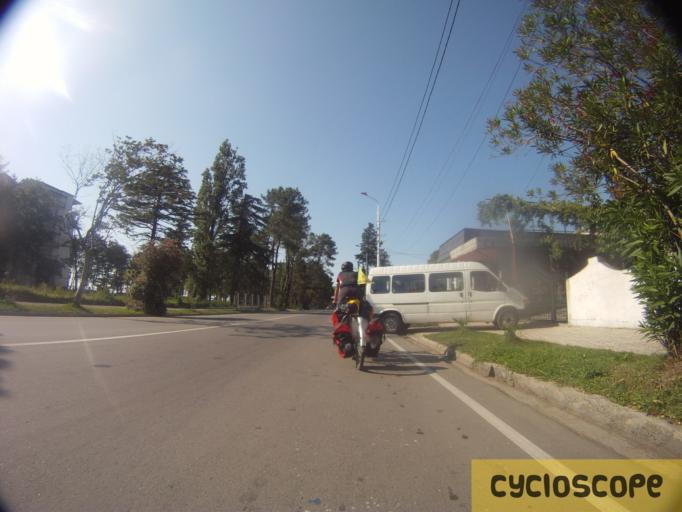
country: GE
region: Ajaria
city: Kobuleti
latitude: 41.8542
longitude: 41.7797
